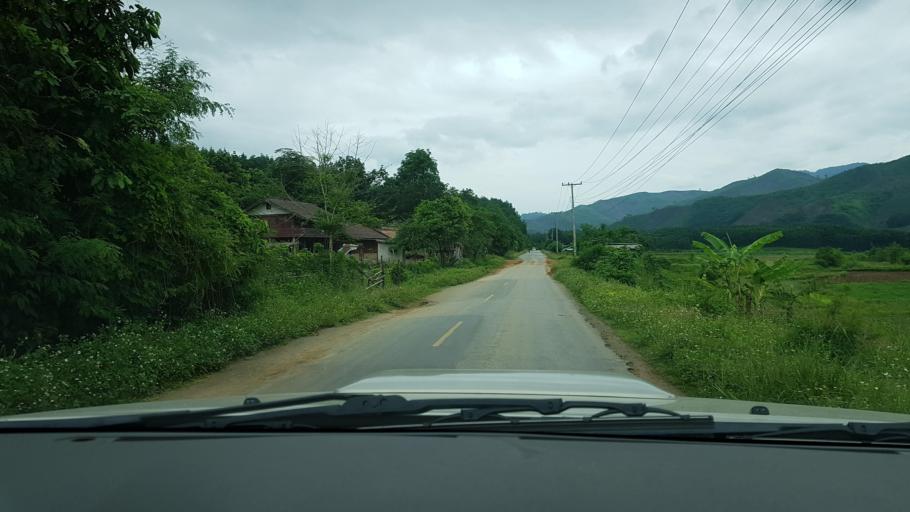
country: LA
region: Loungnamtha
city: Muang Nale
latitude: 20.2408
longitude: 101.5748
